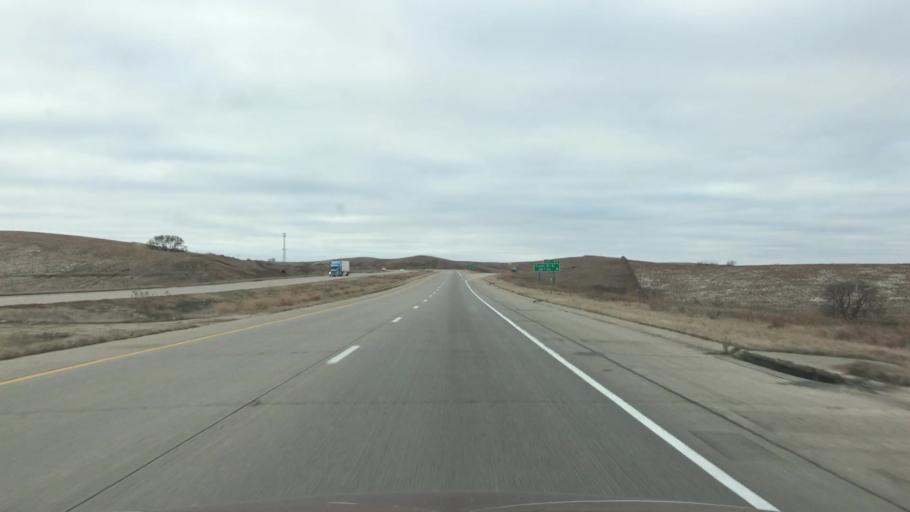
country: US
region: Iowa
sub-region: Woodbury County
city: Sioux City
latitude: 42.5259
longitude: -96.3394
